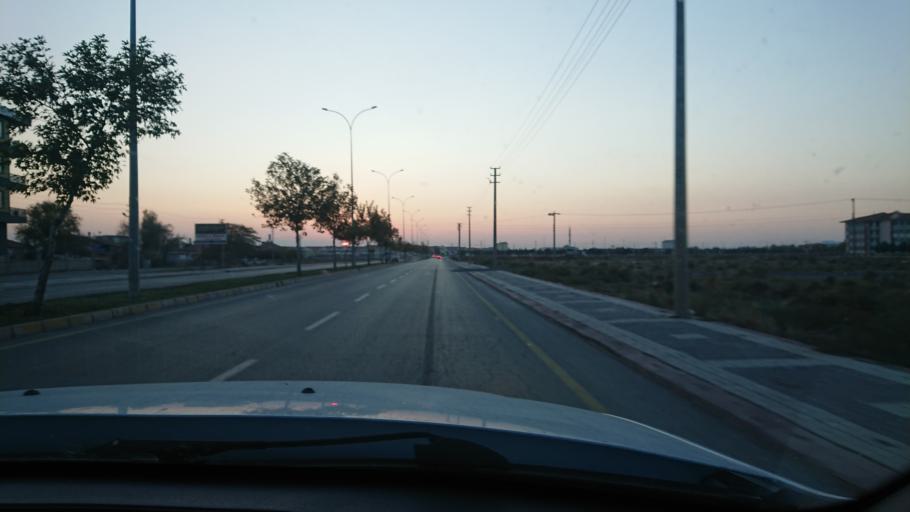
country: TR
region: Aksaray
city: Aksaray
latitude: 38.3583
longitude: 33.9941
